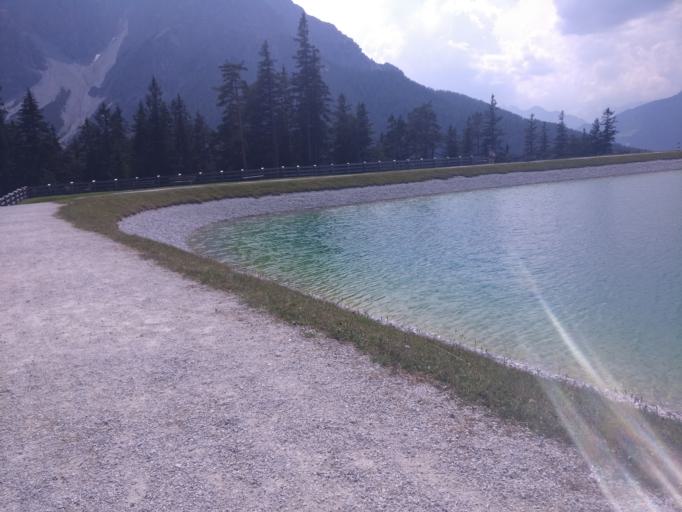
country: AT
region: Tyrol
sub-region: Politischer Bezirk Innsbruck Land
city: Mieders
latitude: 47.1486
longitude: 11.3932
